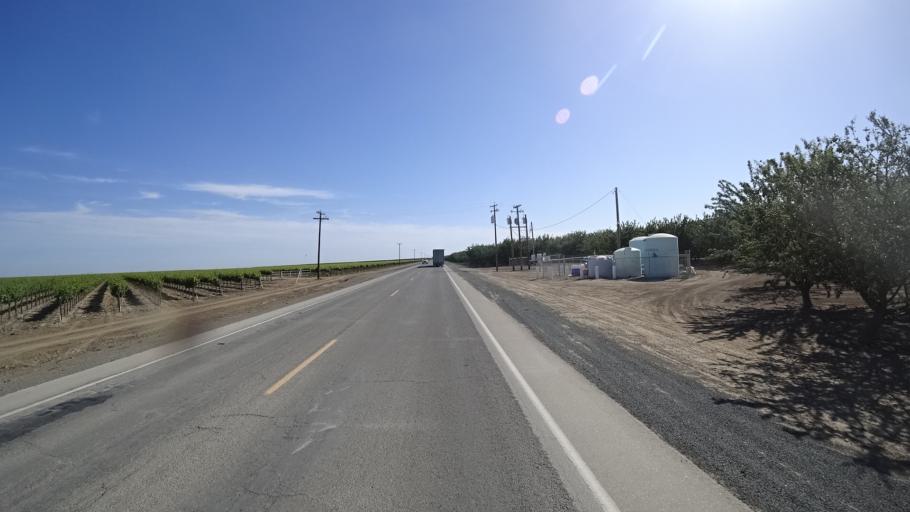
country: US
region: California
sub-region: Fresno County
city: Huron
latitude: 36.1573
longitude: -119.9865
